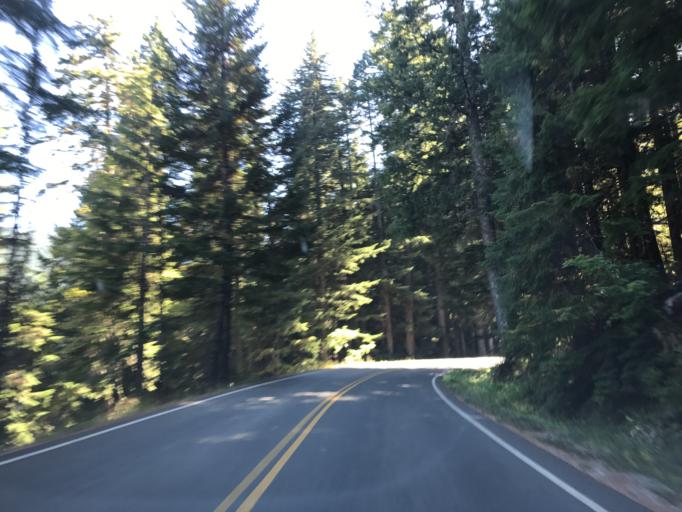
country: US
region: Washington
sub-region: Pierce County
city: Buckley
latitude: 46.7523
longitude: -121.5633
